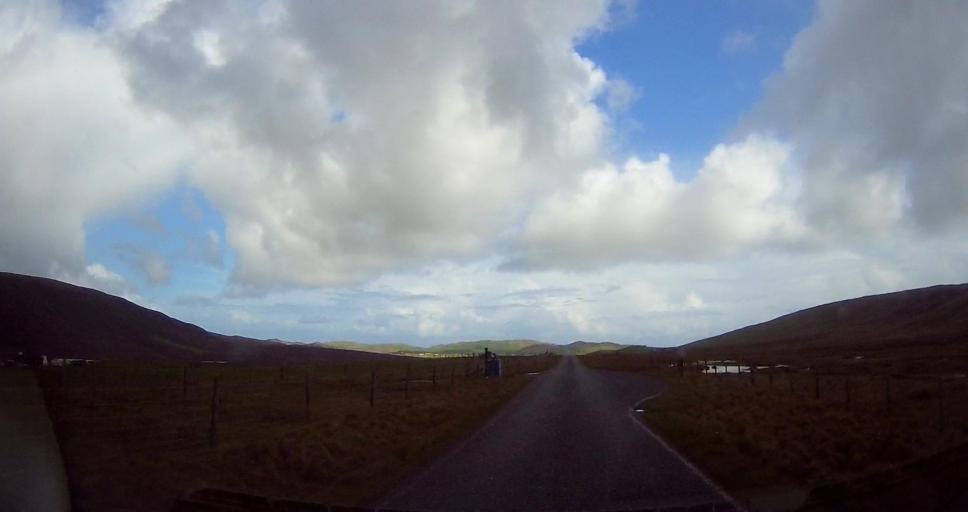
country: GB
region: Scotland
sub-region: Shetland Islands
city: Lerwick
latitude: 60.5602
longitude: -1.3362
